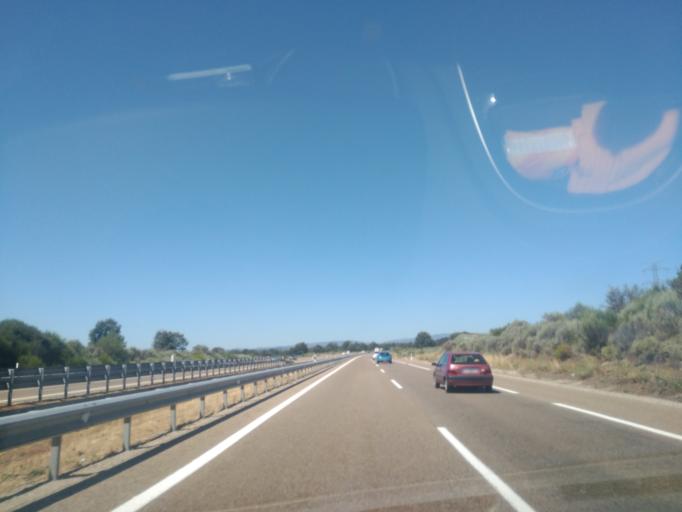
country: ES
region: Castille and Leon
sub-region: Provincia de Zamora
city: Cernadilla
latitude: 42.0228
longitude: -6.3877
